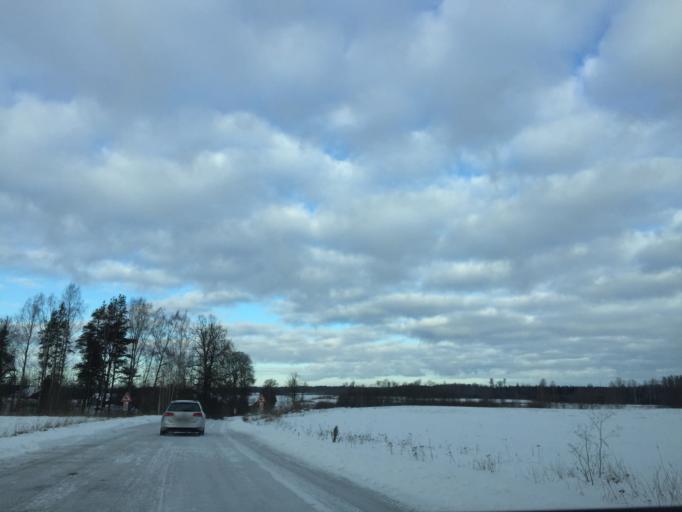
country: LV
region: Lielvarde
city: Lielvarde
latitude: 56.5790
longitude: 24.7358
